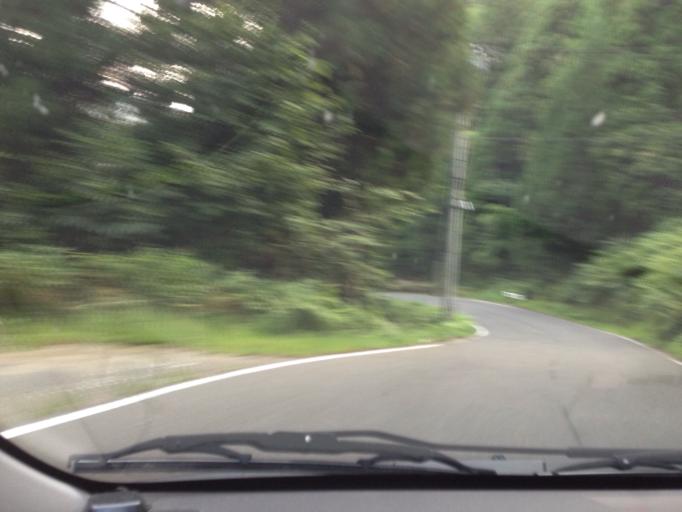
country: JP
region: Fukushima
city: Kitakata
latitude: 37.4842
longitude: 139.6911
